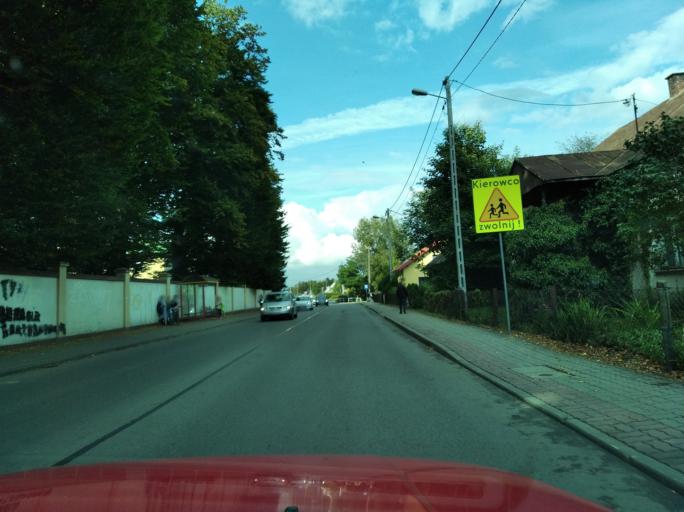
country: PL
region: Subcarpathian Voivodeship
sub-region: Powiat rzeszowski
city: Tyczyn
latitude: 49.9645
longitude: 22.0301
